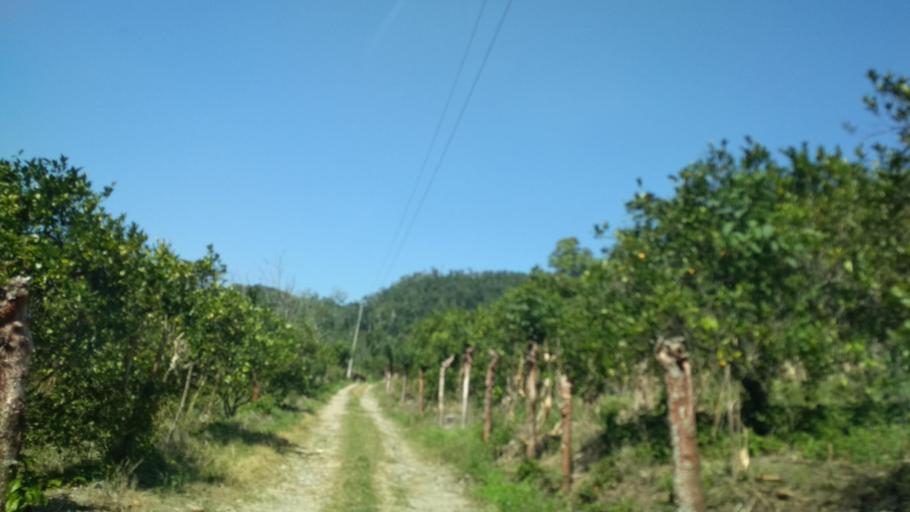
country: MX
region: Veracruz
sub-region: Papantla
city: Polutla
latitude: 20.4858
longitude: -97.2288
